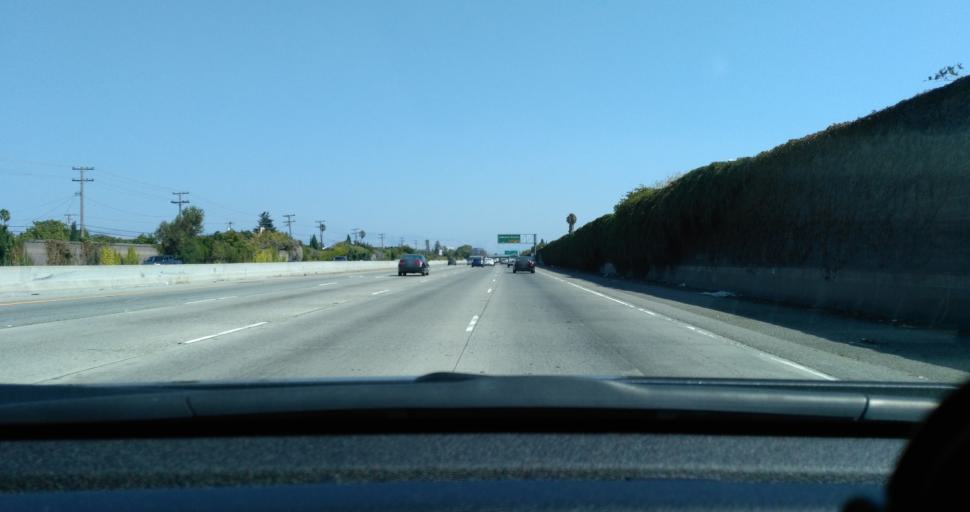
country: US
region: California
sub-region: Santa Clara County
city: Sunnyvale
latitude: 37.3943
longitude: -122.0073
